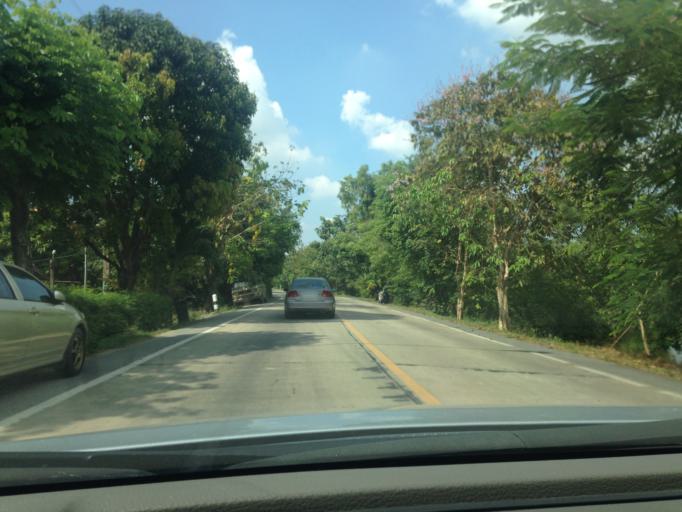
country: TH
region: Pathum Thani
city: Khlong Luang
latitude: 14.0610
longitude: 100.5892
